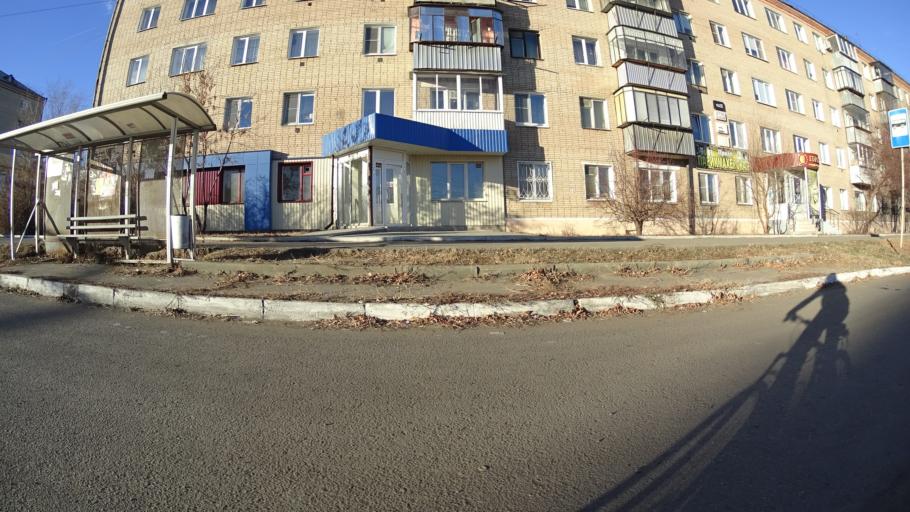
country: RU
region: Chelyabinsk
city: Troitsk
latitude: 54.0801
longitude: 61.5396
